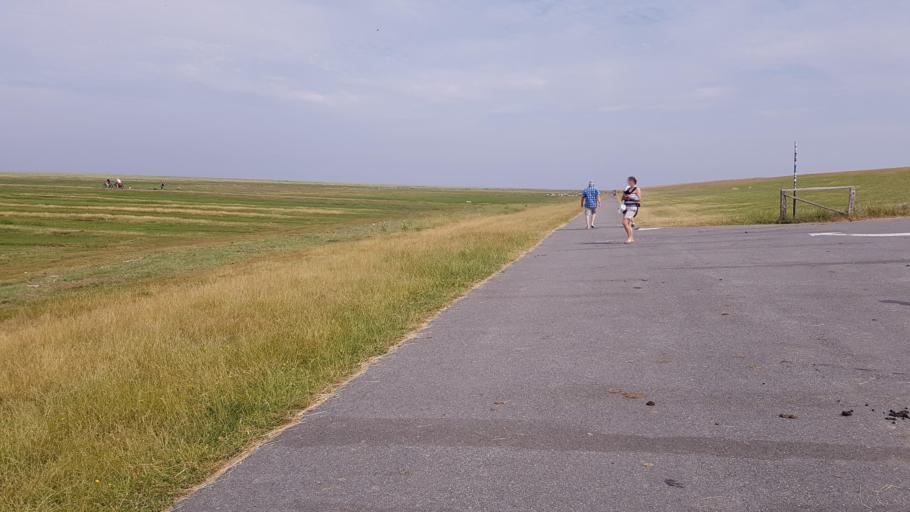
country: DE
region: Schleswig-Holstein
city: Westerhever
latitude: 54.3816
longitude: 8.6484
